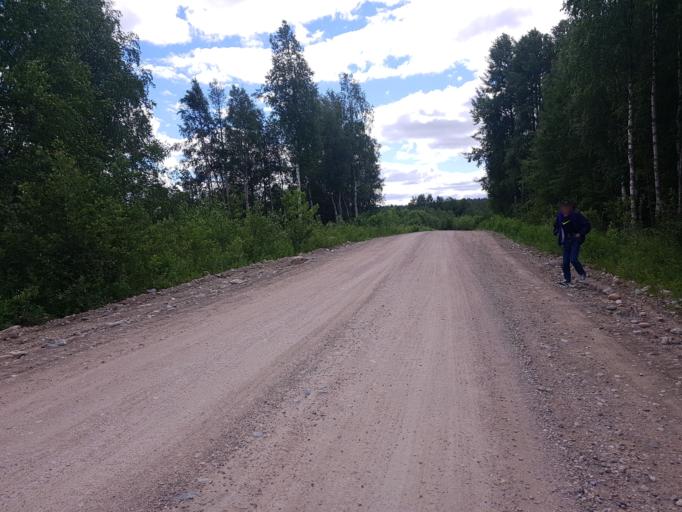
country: RU
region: Republic of Karelia
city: Kostomuksha
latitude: 65.1680
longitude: 30.2964
